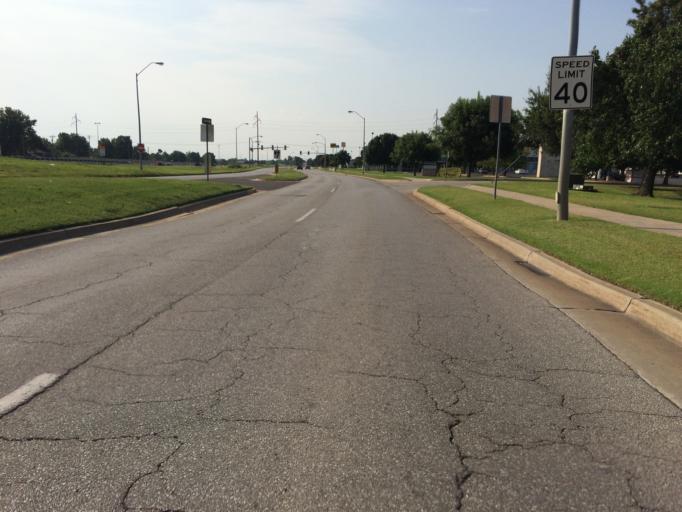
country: US
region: Oklahoma
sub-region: Cleveland County
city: Norman
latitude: 35.2132
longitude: -97.4854
